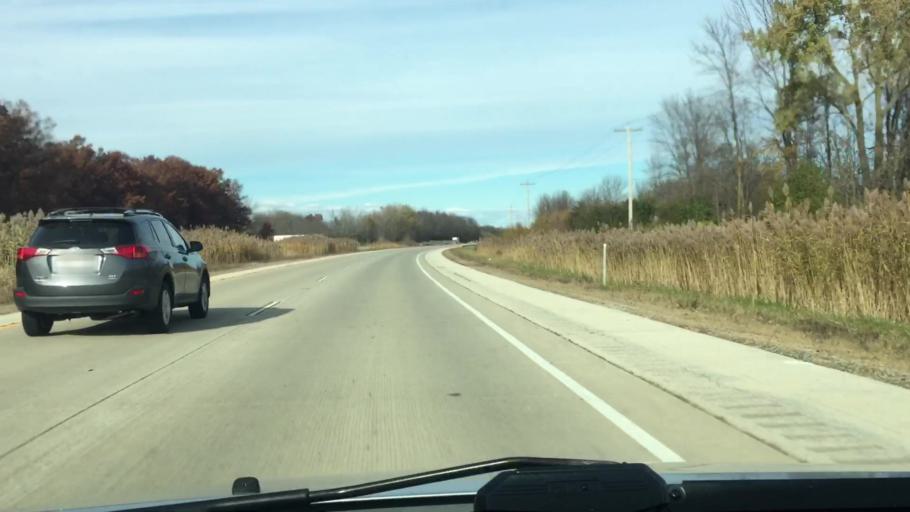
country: US
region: Wisconsin
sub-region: Brown County
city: Bellevue
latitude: 44.5577
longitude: -87.8811
